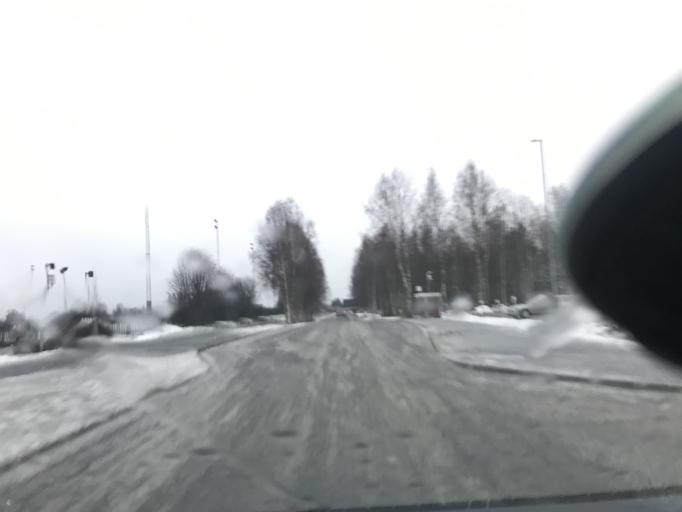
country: SE
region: Norrbotten
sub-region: Lulea Kommun
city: Sodra Sunderbyn
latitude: 65.6596
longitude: 21.9465
